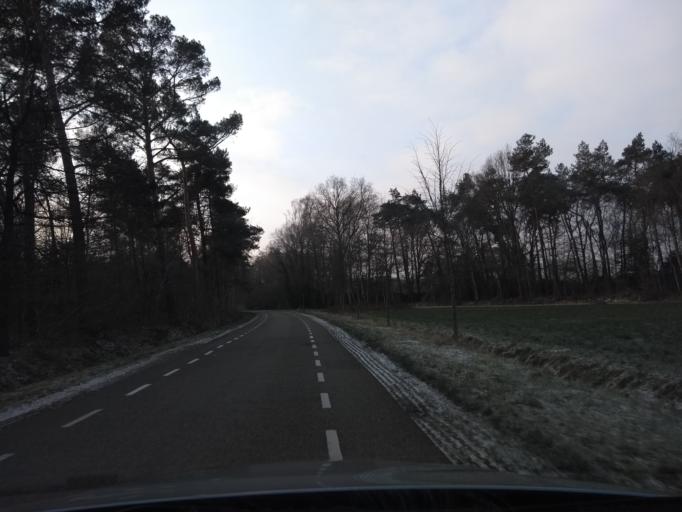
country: NL
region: Overijssel
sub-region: Gemeente Haaksbergen
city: Haaksbergen
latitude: 52.1331
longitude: 6.7454
